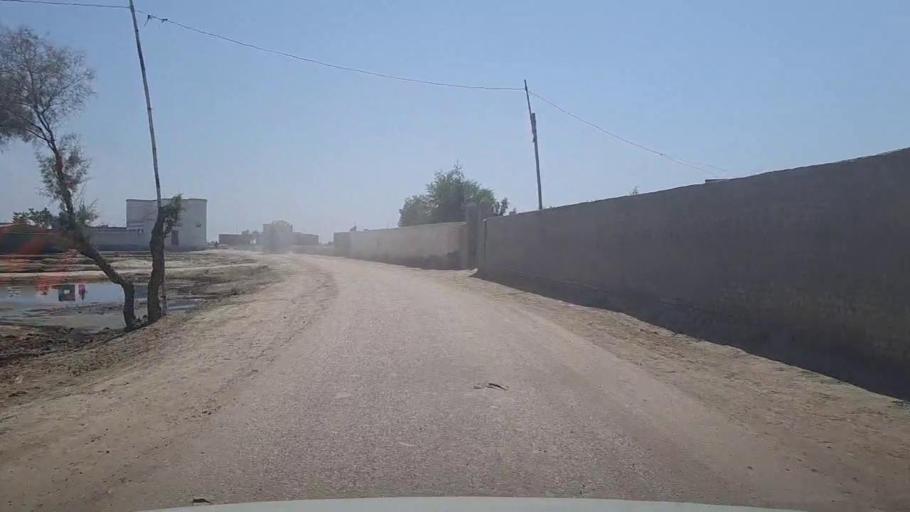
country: PK
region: Sindh
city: Kashmor
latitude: 28.2881
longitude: 69.4358
